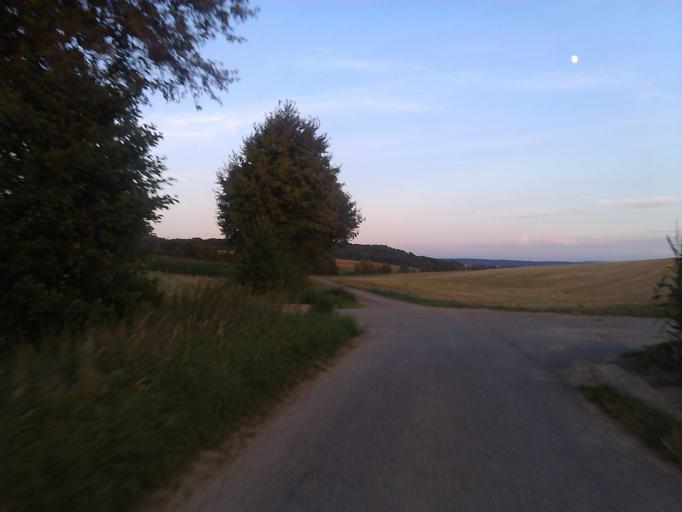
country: DE
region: Baden-Wuerttemberg
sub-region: Regierungsbezirk Stuttgart
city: Ittlingen
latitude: 49.1863
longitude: 8.8760
